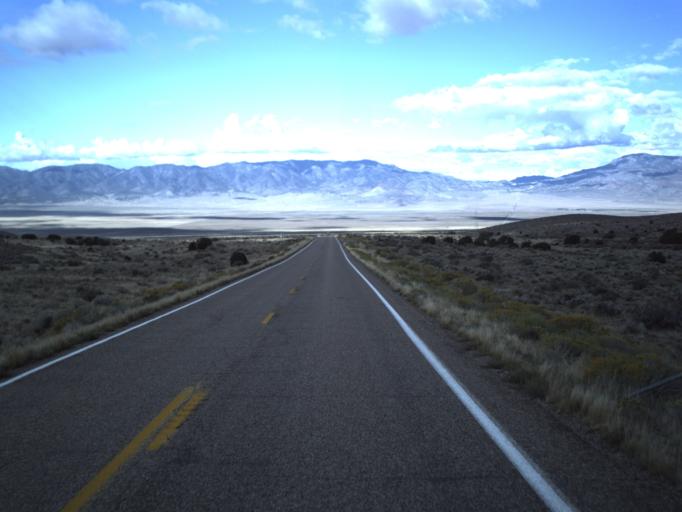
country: US
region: Utah
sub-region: Beaver County
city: Milford
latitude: 38.4342
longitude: -113.2891
